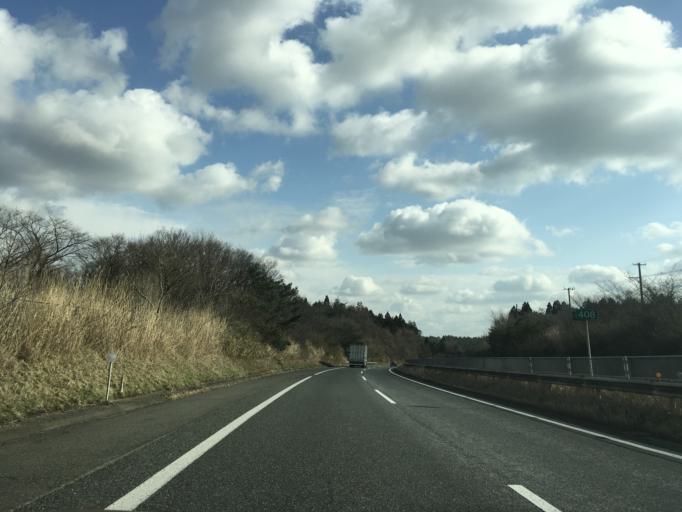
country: JP
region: Iwate
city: Ichinoseki
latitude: 38.8362
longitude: 141.1000
